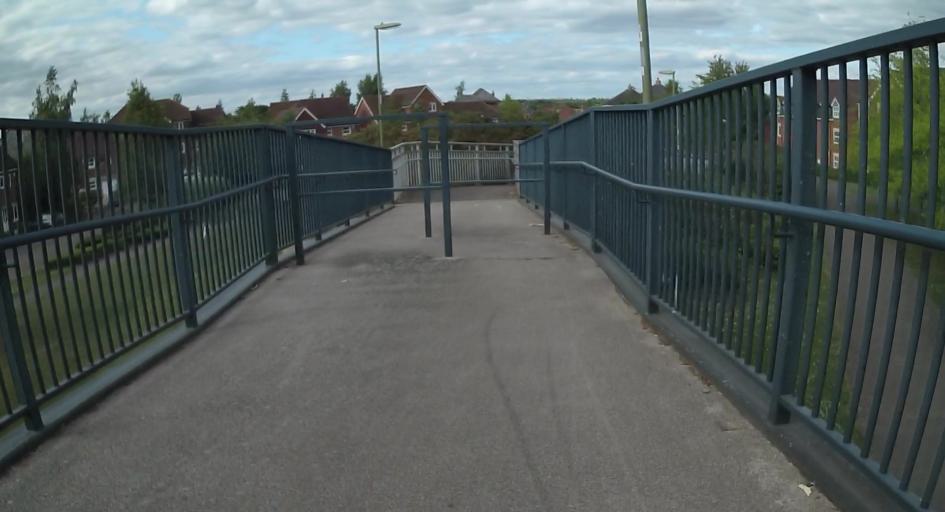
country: GB
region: England
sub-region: Hampshire
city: Fleet
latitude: 51.2897
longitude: -0.8484
